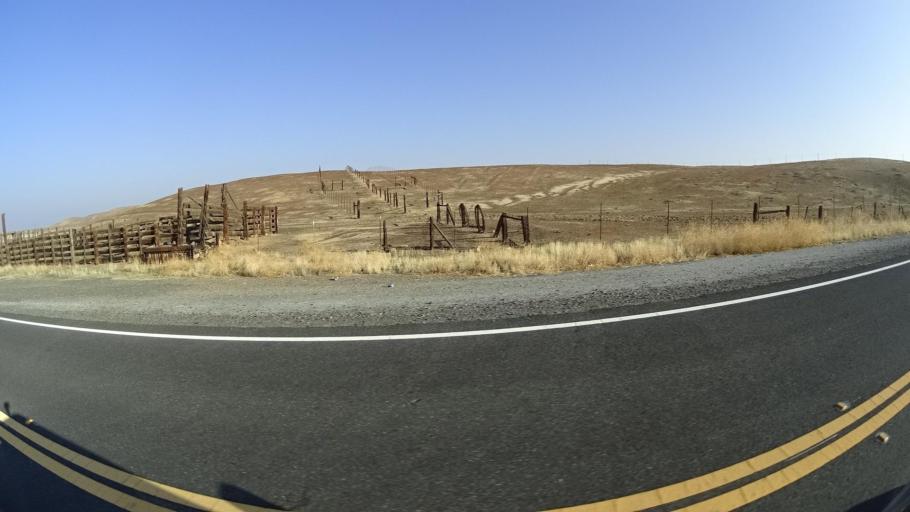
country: US
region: California
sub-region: Tulare County
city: Richgrove
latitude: 35.7601
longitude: -119.0283
